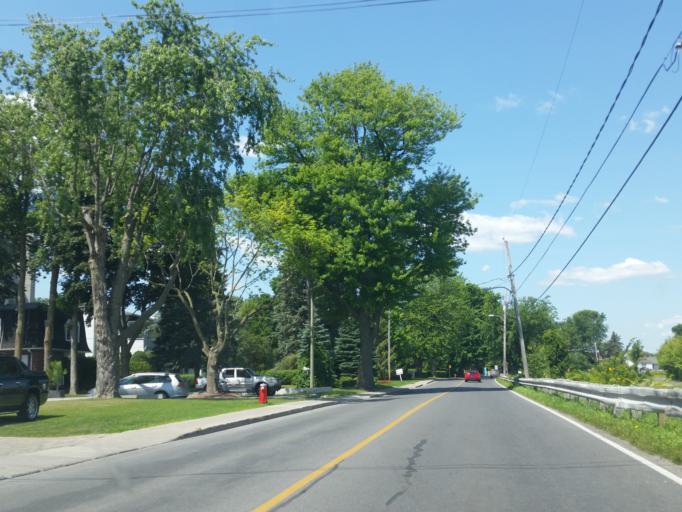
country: CA
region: Quebec
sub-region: Monteregie
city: Saint-Jean-sur-Richelieu
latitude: 45.3195
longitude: -73.2590
